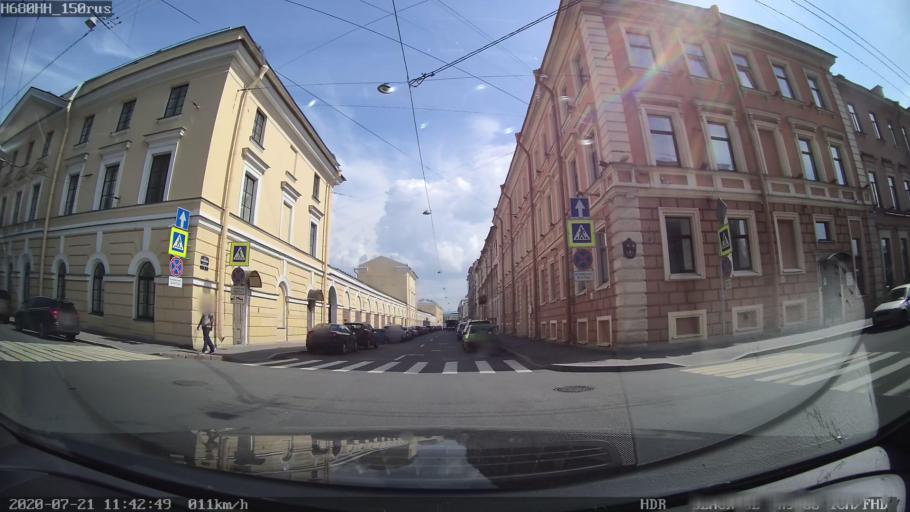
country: RU
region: St.-Petersburg
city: Saint Petersburg
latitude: 59.9317
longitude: 30.2962
